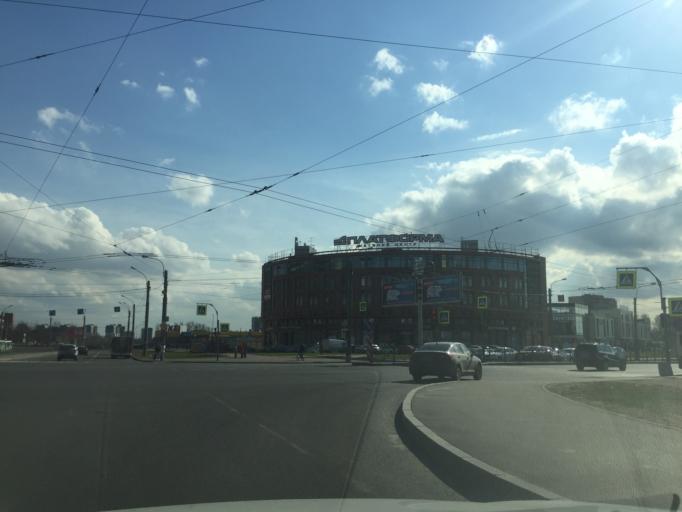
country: RU
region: St.-Petersburg
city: Krasnogvargeisky
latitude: 59.9337
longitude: 30.4352
